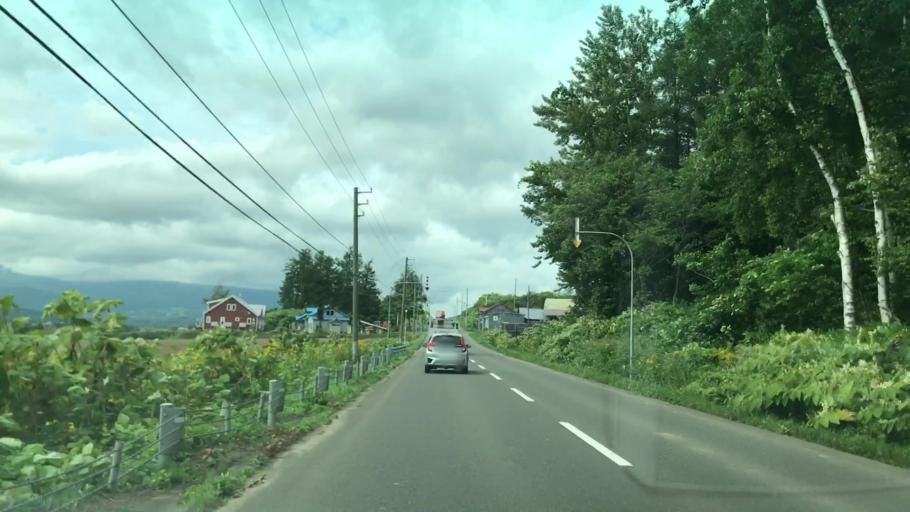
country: JP
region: Hokkaido
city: Niseko Town
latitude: 42.9322
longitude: 140.7941
